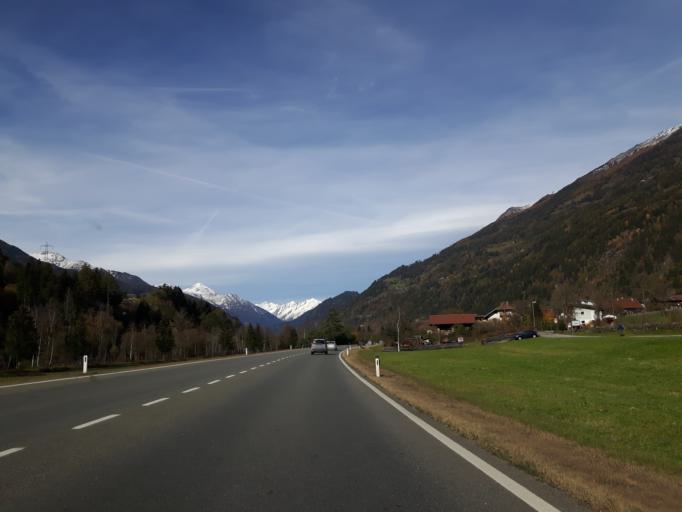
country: AT
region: Tyrol
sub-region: Politischer Bezirk Lienz
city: Ainet
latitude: 46.8609
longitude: 12.6908
